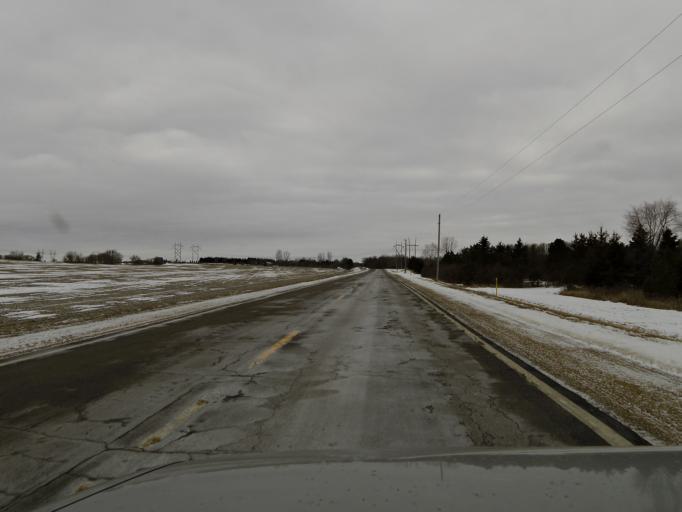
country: US
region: Minnesota
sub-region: Washington County
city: Cottage Grove
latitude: 44.8251
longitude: -92.8906
